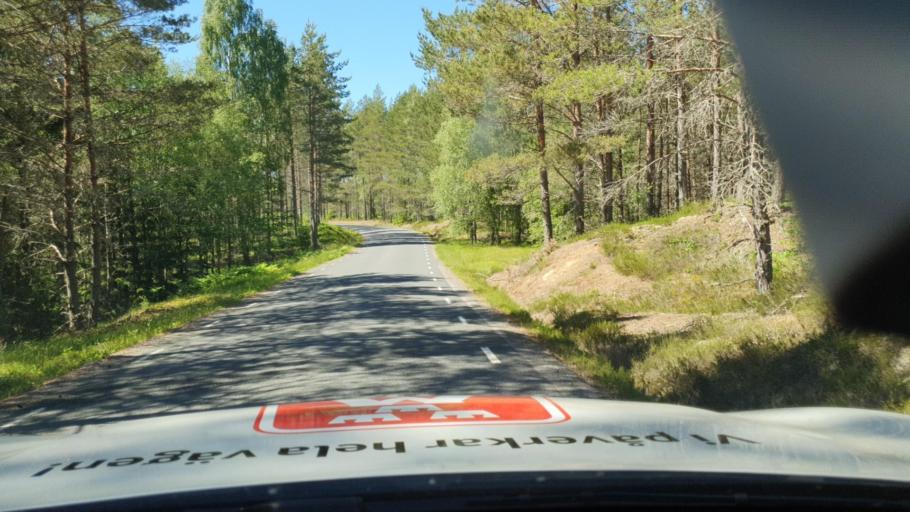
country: SE
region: Joenkoeping
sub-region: Habo Kommun
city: Habo
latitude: 57.9863
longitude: 14.0176
